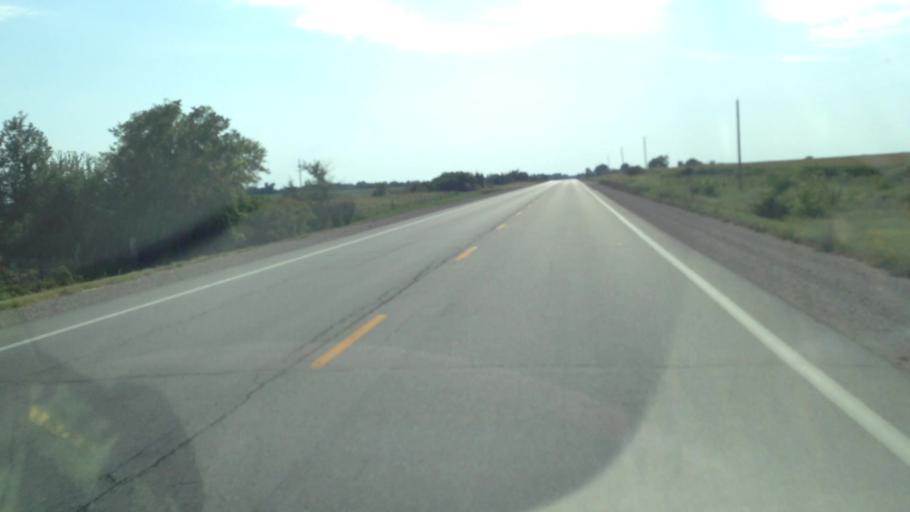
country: US
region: Kansas
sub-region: Anderson County
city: Garnett
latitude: 38.0816
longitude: -95.2136
